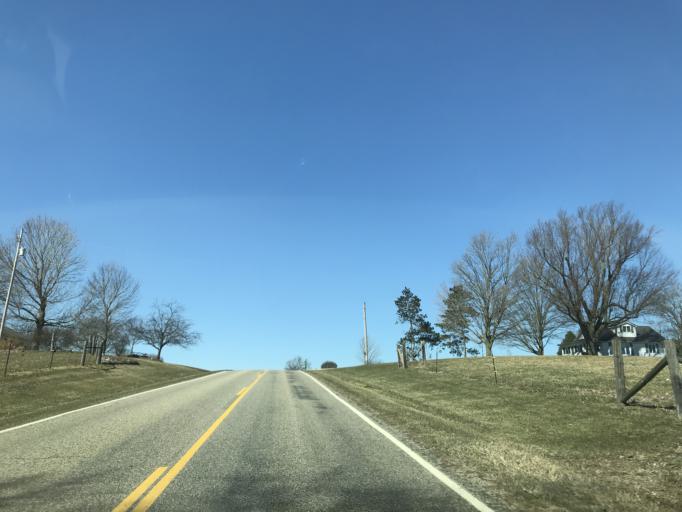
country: US
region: Michigan
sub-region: Hillsdale County
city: Jonesville
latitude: 41.9855
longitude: -84.7113
